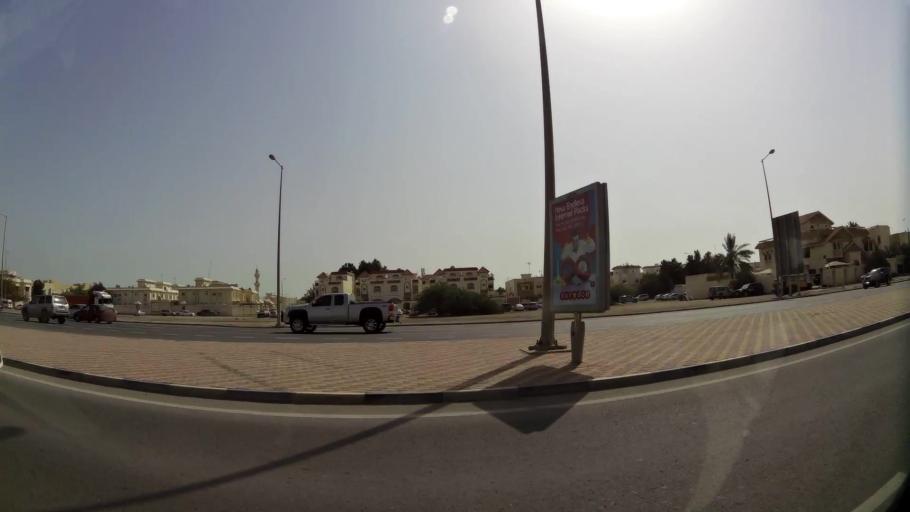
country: QA
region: Baladiyat ad Dawhah
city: Doha
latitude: 25.2513
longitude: 51.5242
